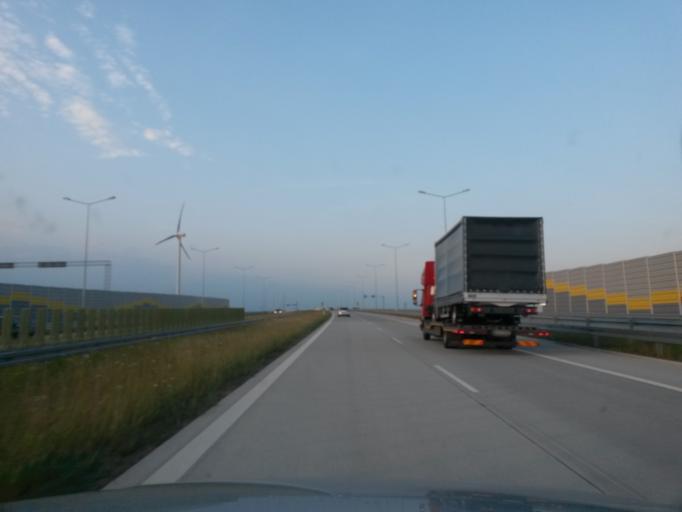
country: PL
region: Lodz Voivodeship
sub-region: Powiat sieradzki
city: Zloczew
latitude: 51.3989
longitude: 18.6161
